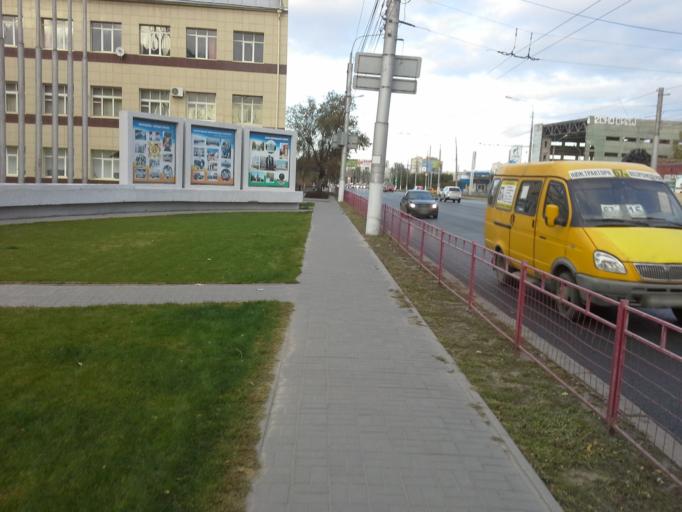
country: RU
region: Volgograd
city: Vodstroy
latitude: 48.8051
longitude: 44.6069
